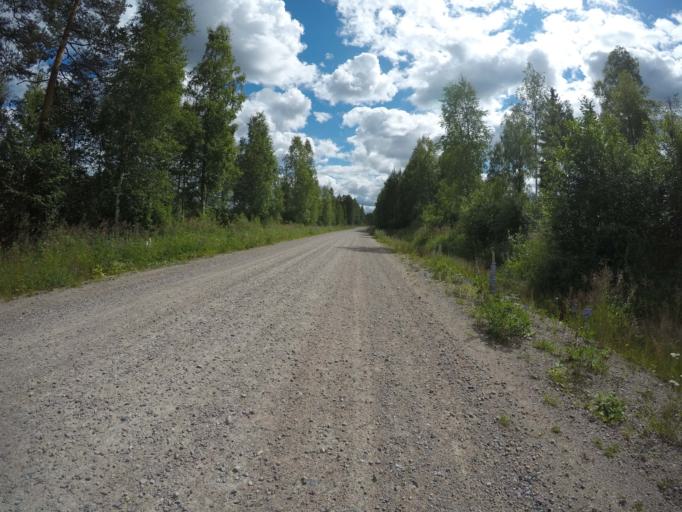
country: SE
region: Vaermland
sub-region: Filipstads Kommun
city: Lesjofors
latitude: 60.1263
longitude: 14.4290
